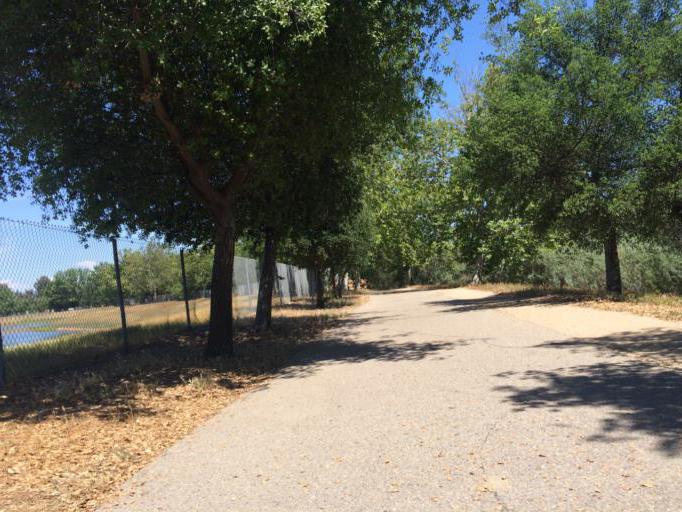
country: US
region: California
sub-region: Fresno County
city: Clovis
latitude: 36.8418
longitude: -119.7056
